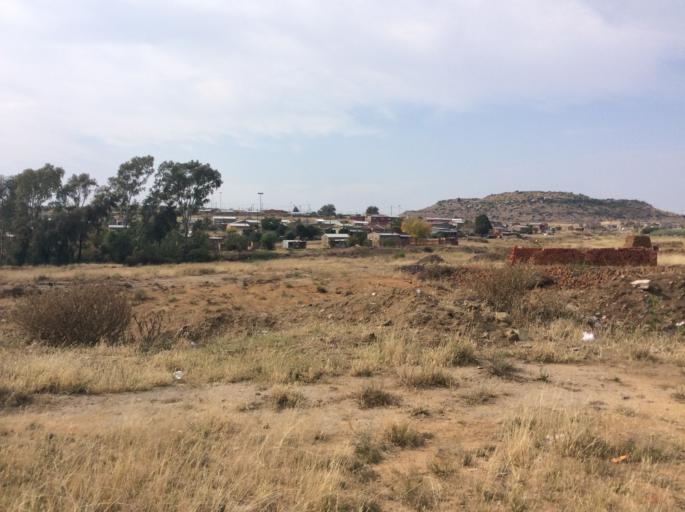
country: ZA
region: Orange Free State
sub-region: Xhariep District Municipality
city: Dewetsdorp
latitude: -29.5891
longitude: 26.6769
